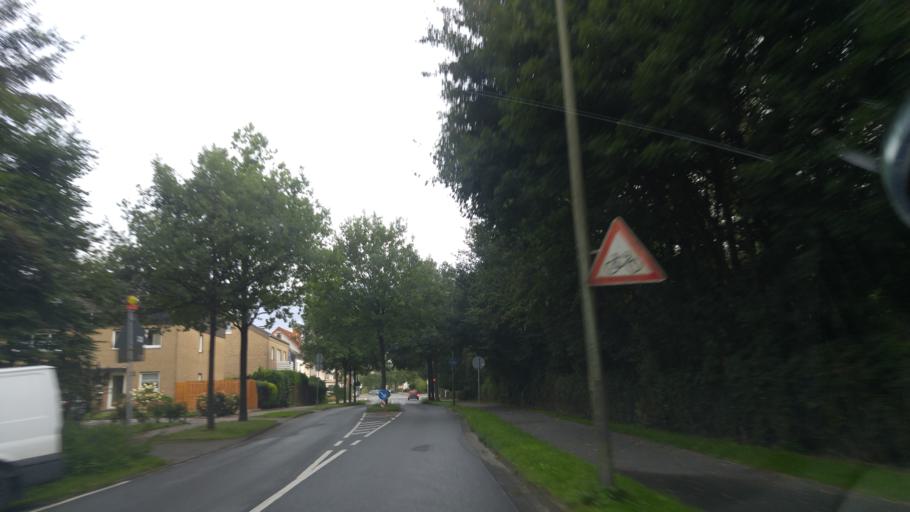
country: DE
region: North Rhine-Westphalia
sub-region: Regierungsbezirk Detmold
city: Bielefeld
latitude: 52.0586
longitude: 8.5270
